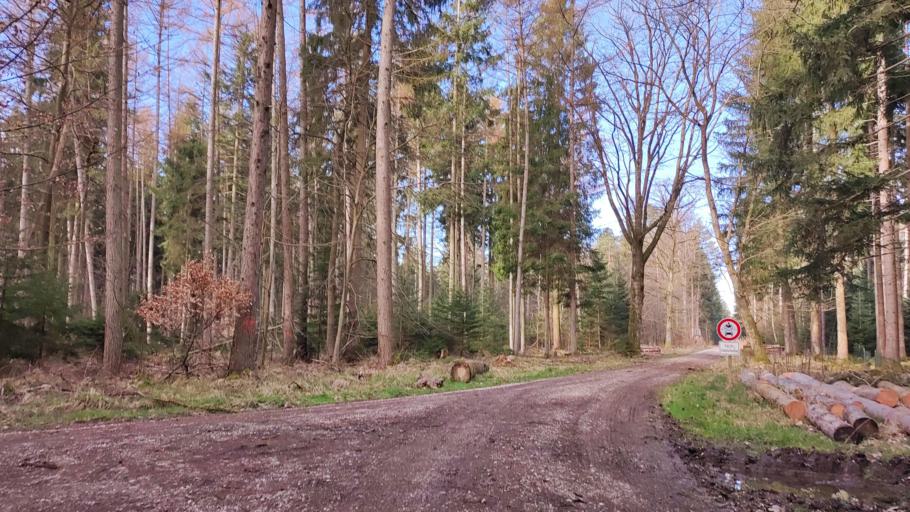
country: DE
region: Bavaria
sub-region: Swabia
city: Landensberg
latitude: 48.4297
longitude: 10.5661
